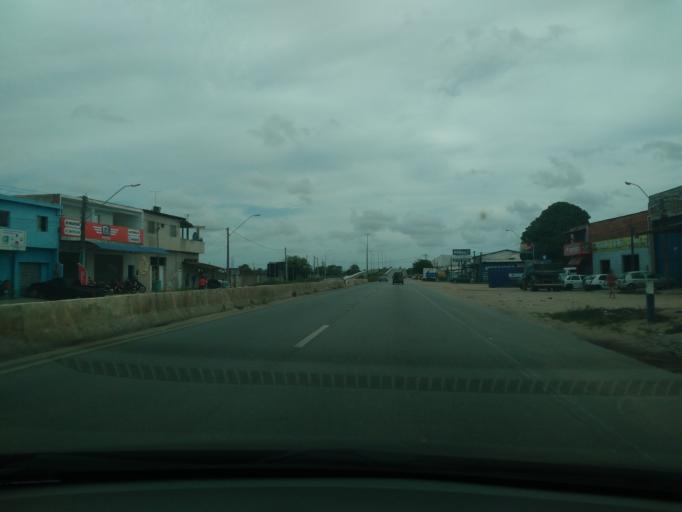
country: BR
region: Alagoas
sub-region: Rio Largo
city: Rio Largo
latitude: -9.5098
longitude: -35.8074
